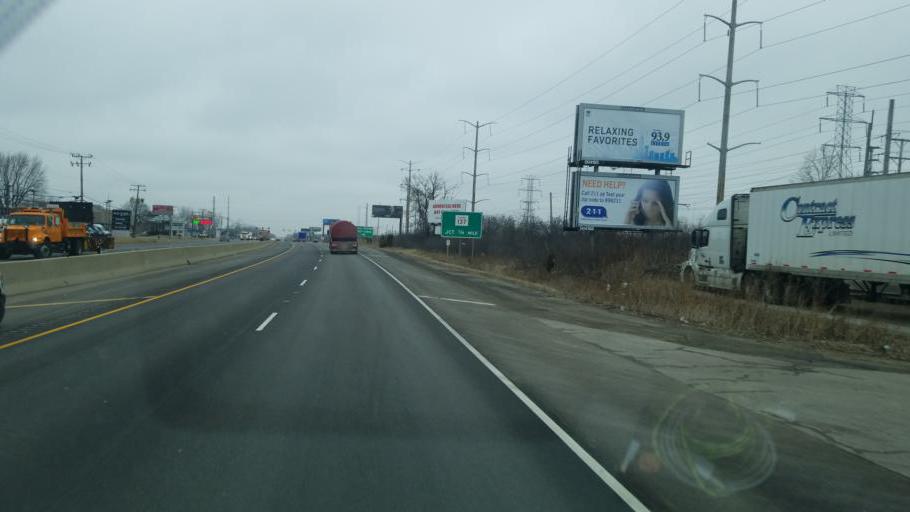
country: US
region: Illinois
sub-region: Lake County
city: Knollwood
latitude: 42.3048
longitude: -87.8756
